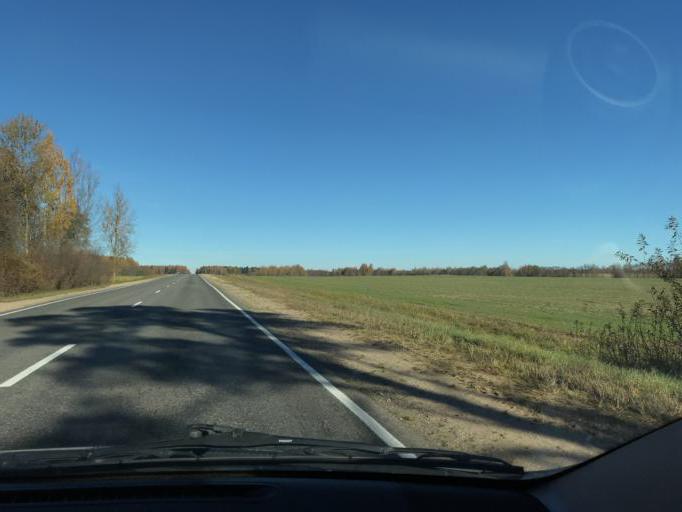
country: BY
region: Vitebsk
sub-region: Ushatski Rayon
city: Ushachy
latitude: 55.0809
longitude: 28.7554
